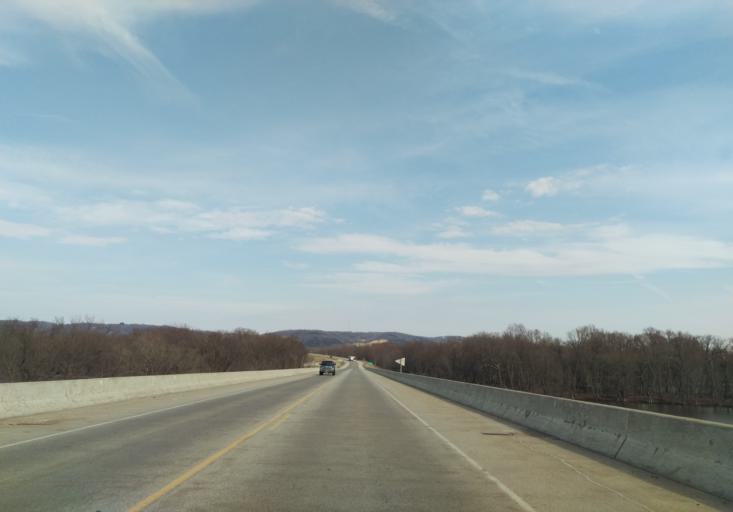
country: US
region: Wisconsin
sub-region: Crawford County
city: Prairie du Chien
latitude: 43.0441
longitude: -91.1731
